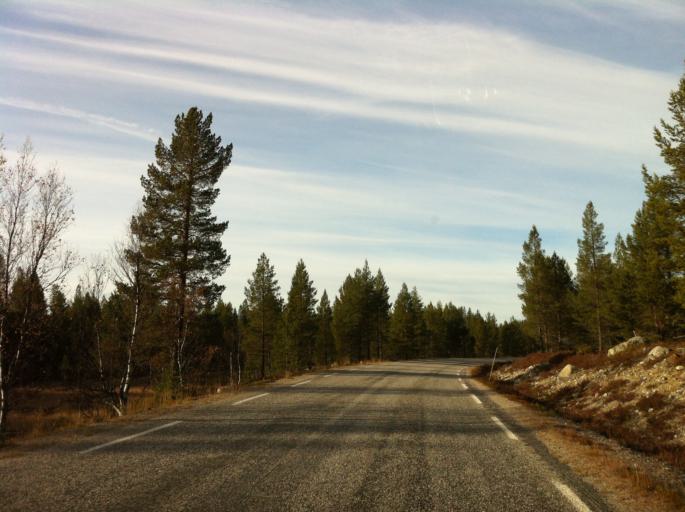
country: NO
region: Hedmark
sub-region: Engerdal
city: Engerdal
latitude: 62.1174
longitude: 12.0144
